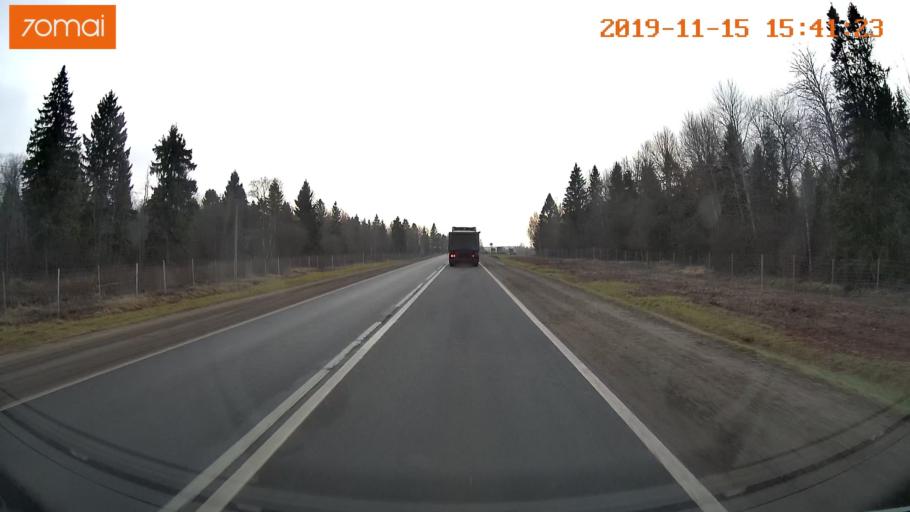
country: RU
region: Jaroslavl
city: Danilov
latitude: 58.0013
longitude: 40.0486
